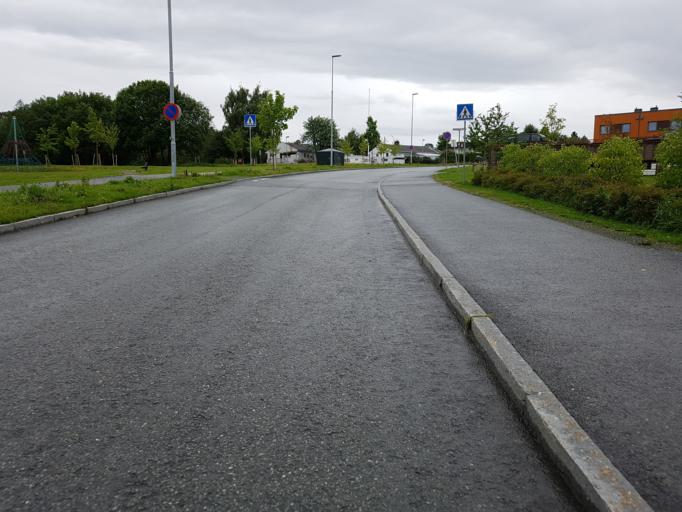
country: NO
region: Sor-Trondelag
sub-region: Trondheim
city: Trondheim
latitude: 63.4136
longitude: 10.4805
